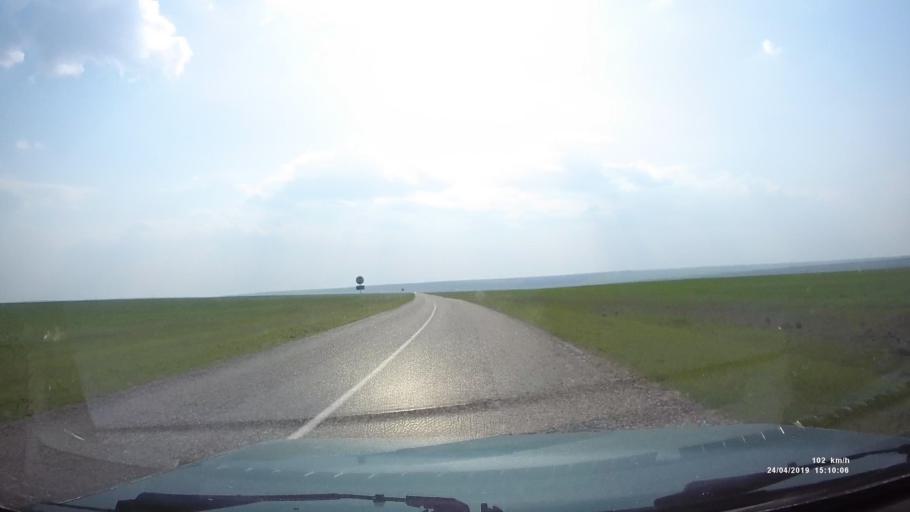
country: RU
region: Rostov
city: Remontnoye
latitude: 46.5525
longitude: 43.3479
